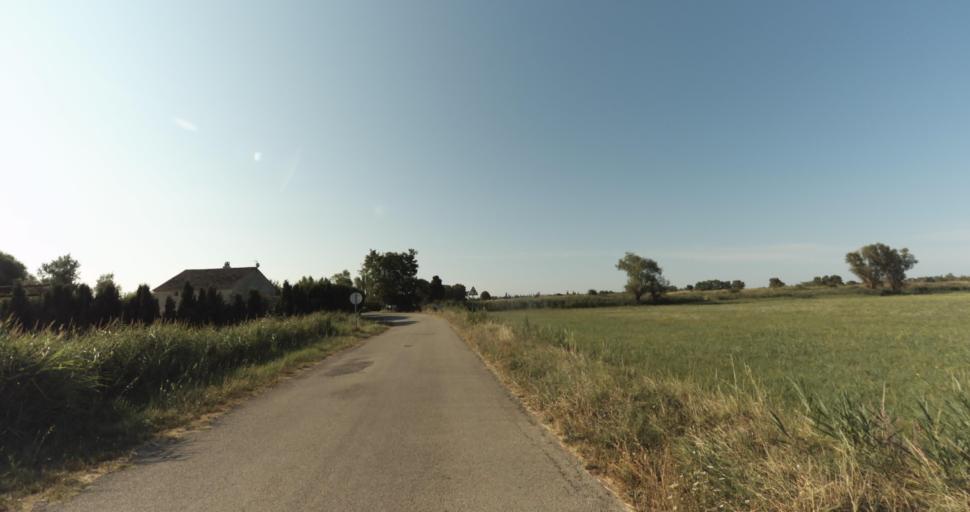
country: FR
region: Provence-Alpes-Cote d'Azur
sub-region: Departement du Vaucluse
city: Sarrians
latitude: 44.0485
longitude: 4.9516
